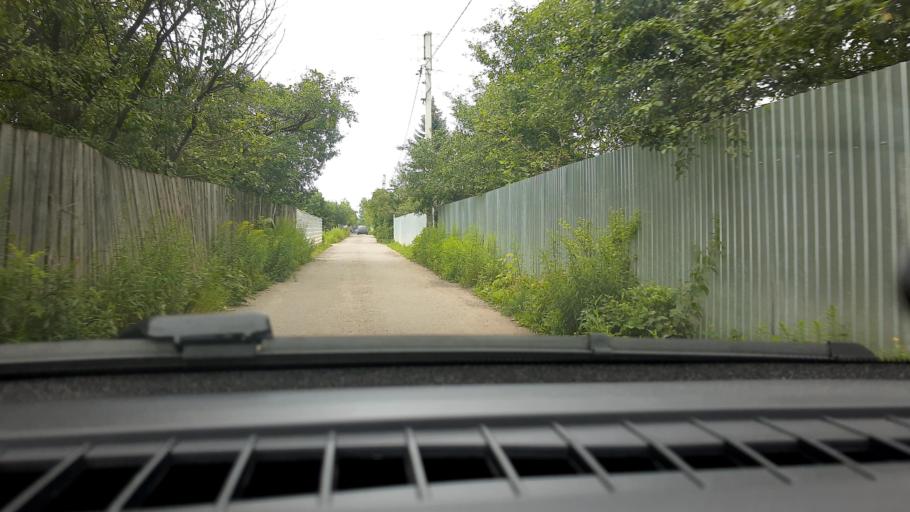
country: RU
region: Nizjnij Novgorod
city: Gorbatovka
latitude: 56.2445
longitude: 43.8181
